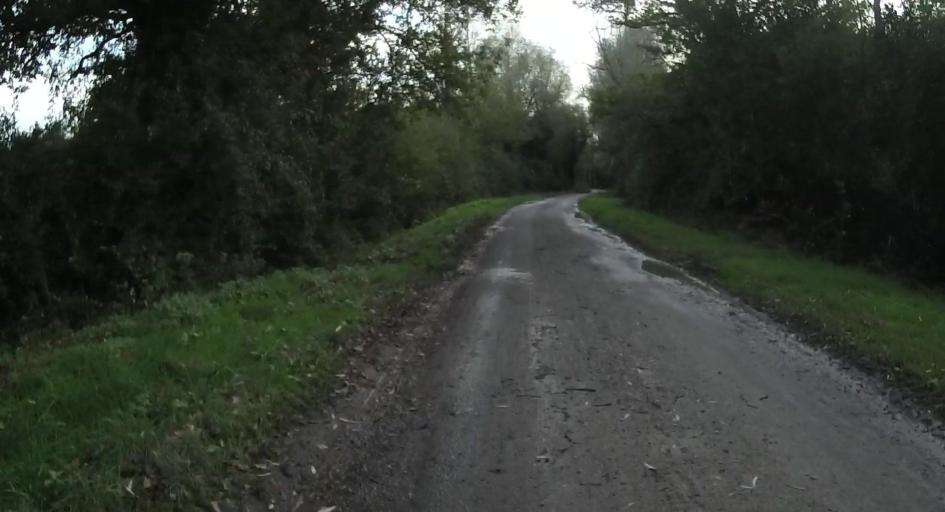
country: GB
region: England
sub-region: Wokingham
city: Swallowfield
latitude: 51.3754
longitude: -0.9612
